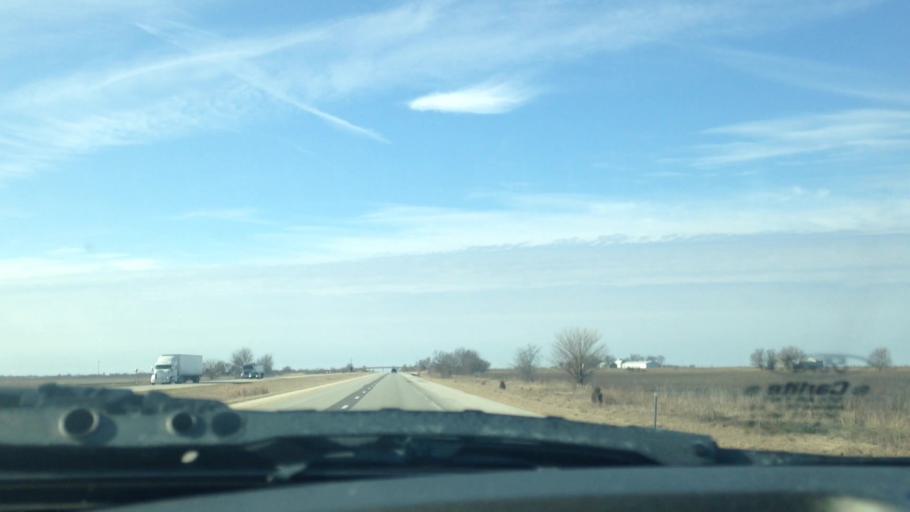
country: US
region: Illinois
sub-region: Ford County
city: Paxton
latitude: 40.4988
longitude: -88.0899
